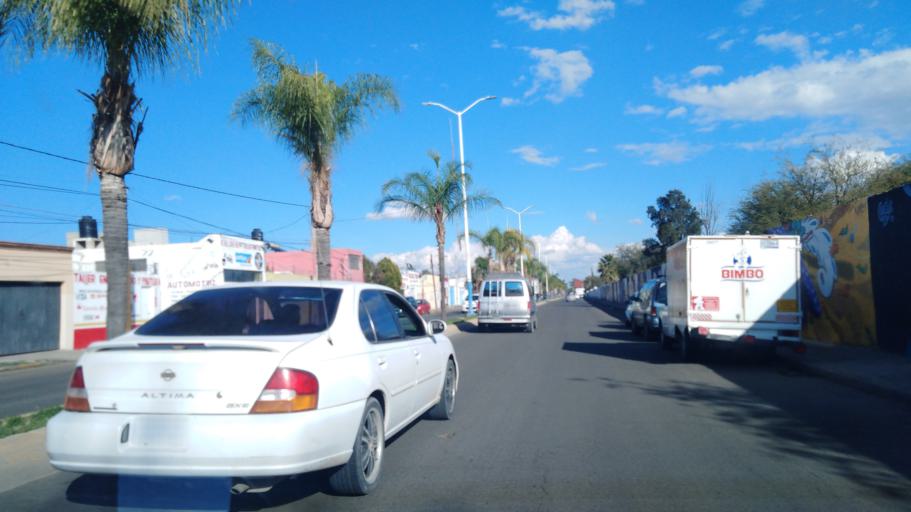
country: MX
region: Durango
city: Victoria de Durango
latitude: 24.0299
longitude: -104.6402
